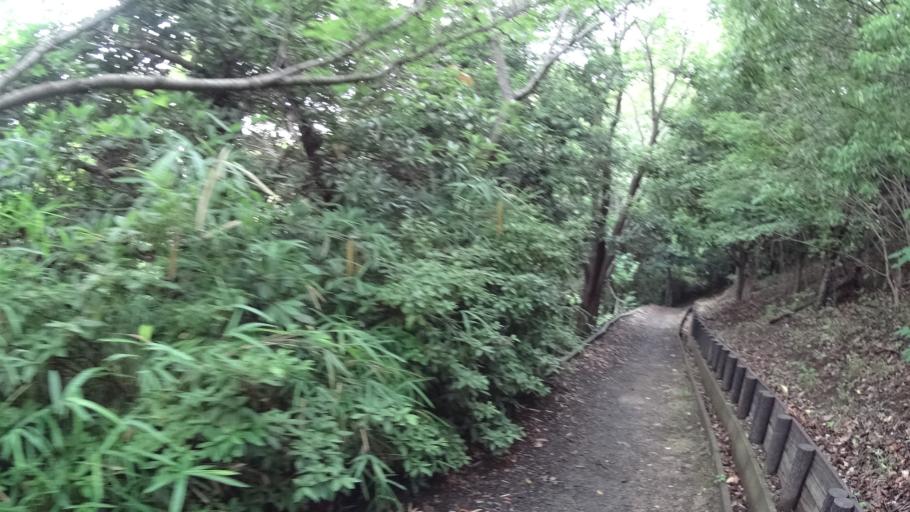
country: JP
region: Kanagawa
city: Zushi
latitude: 35.3563
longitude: 139.6108
